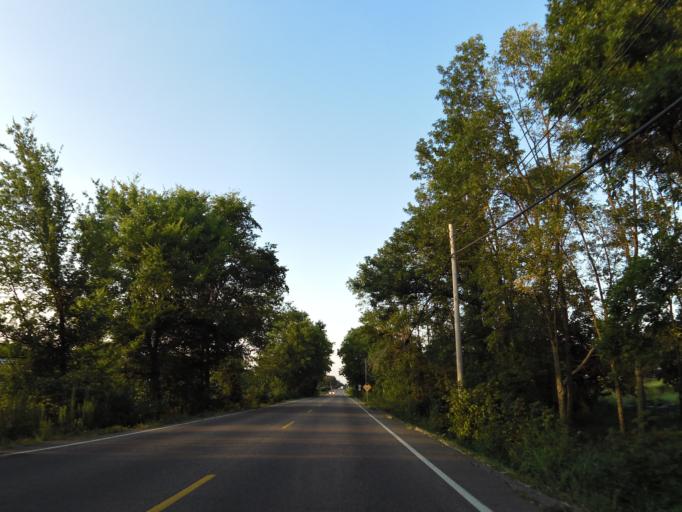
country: US
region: Tennessee
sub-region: Monroe County
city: Sweetwater
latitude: 35.6676
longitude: -84.4098
